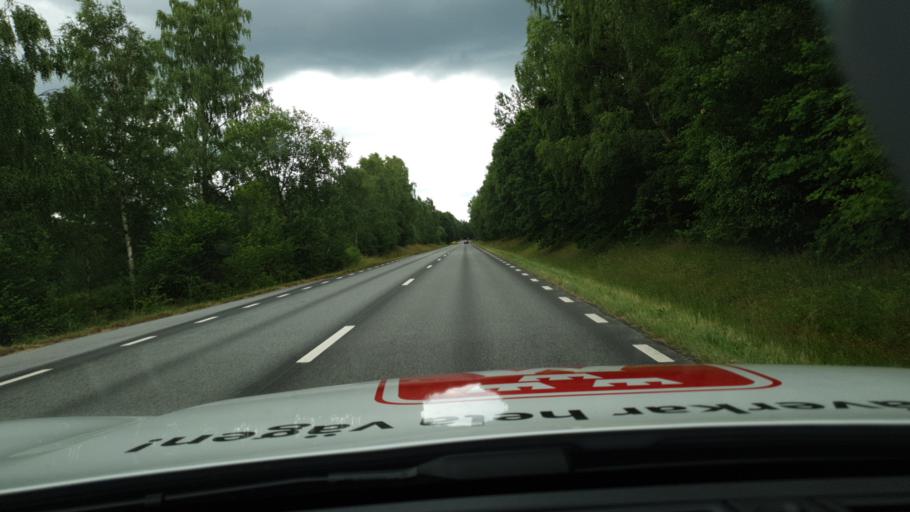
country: SE
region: Skane
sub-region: Hassleholms Kommun
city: Tormestorp
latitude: 56.1082
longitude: 13.7334
